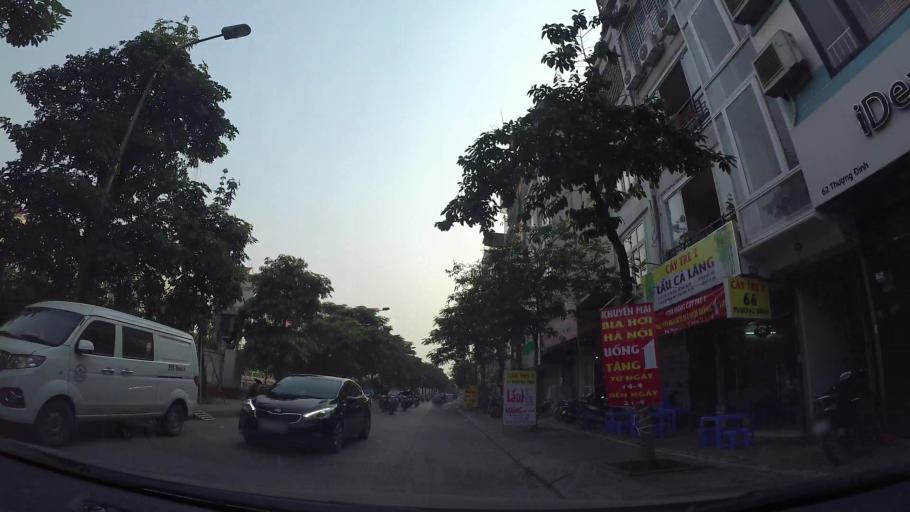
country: VN
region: Ha Noi
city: Thanh Xuan
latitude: 20.9996
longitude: 105.8177
